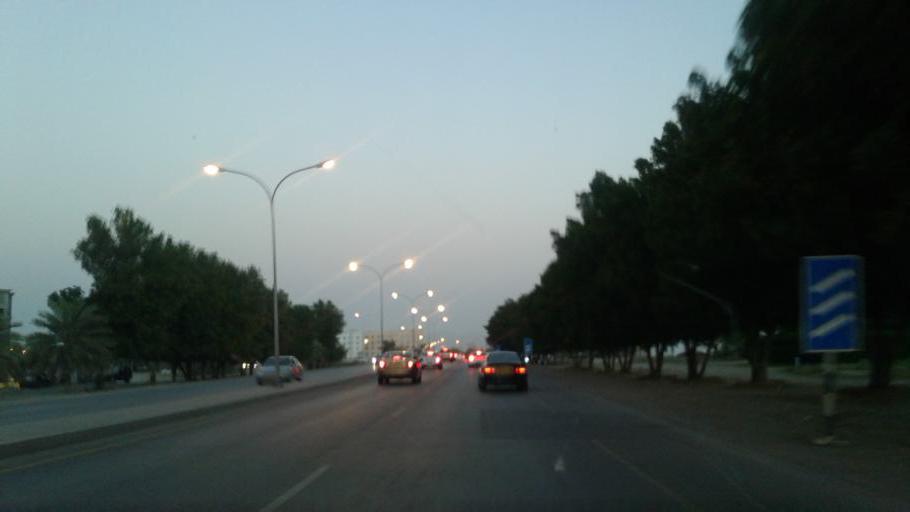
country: OM
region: Muhafazat Masqat
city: As Sib al Jadidah
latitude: 23.6116
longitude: 58.2388
